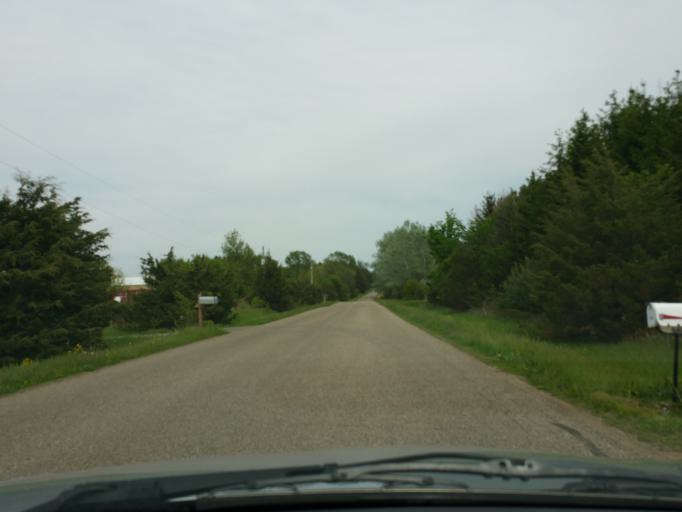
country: US
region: Wisconsin
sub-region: Saint Croix County
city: Hudson
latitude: 44.9488
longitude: -92.6896
